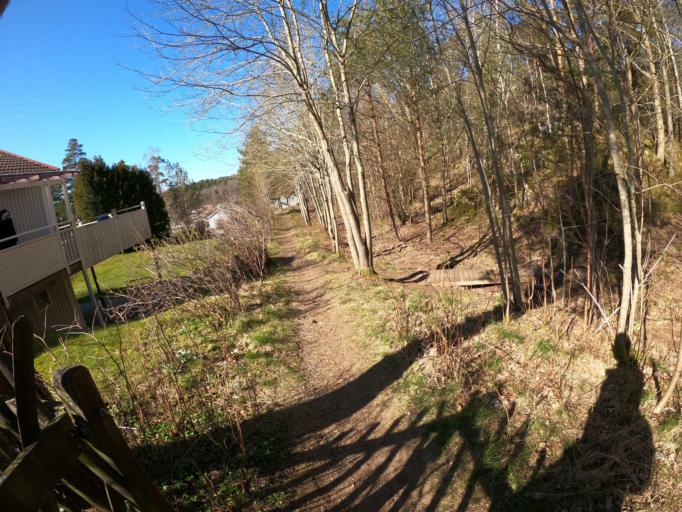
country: SE
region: Vaestra Goetaland
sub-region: Harryda Kommun
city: Molnlycke
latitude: 57.6452
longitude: 12.1127
